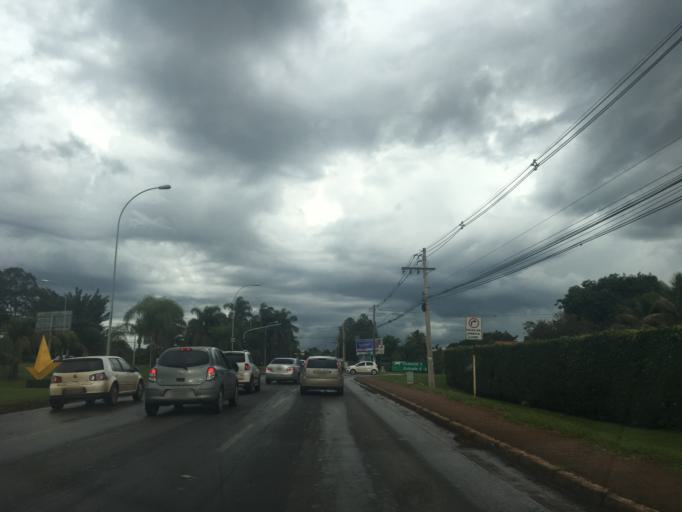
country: BR
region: Federal District
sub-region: Brasilia
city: Brasilia
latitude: -15.7238
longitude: -47.8937
